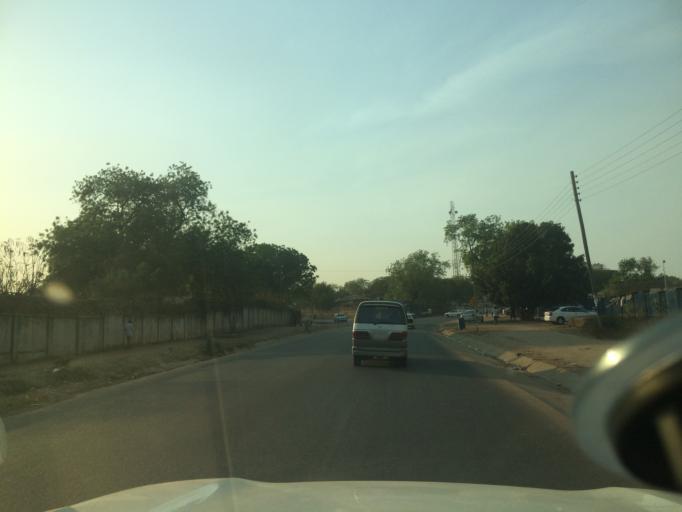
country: SS
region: Central Equatoria
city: Juba
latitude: 4.8469
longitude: 31.6059
